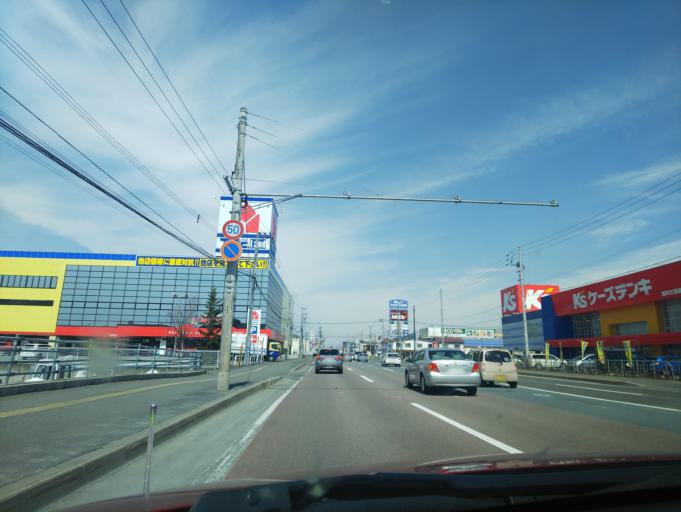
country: JP
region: Hokkaido
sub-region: Asahikawa-shi
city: Asahikawa
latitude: 43.7733
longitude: 142.3826
